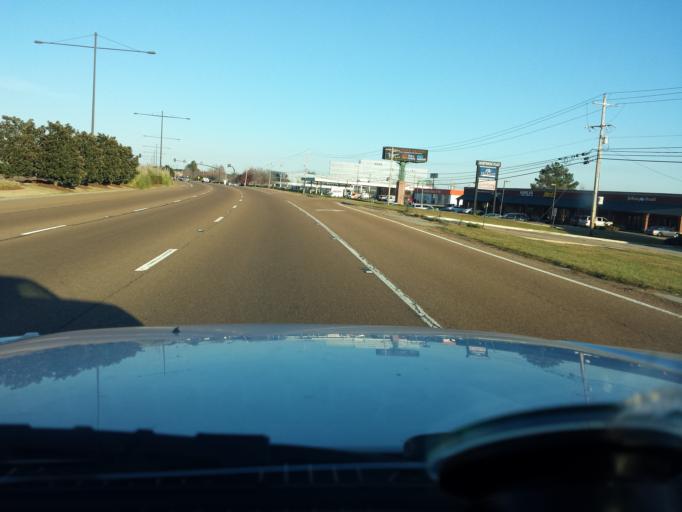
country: US
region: Mississippi
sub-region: Rankin County
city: Flowood
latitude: 32.3289
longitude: -90.1161
